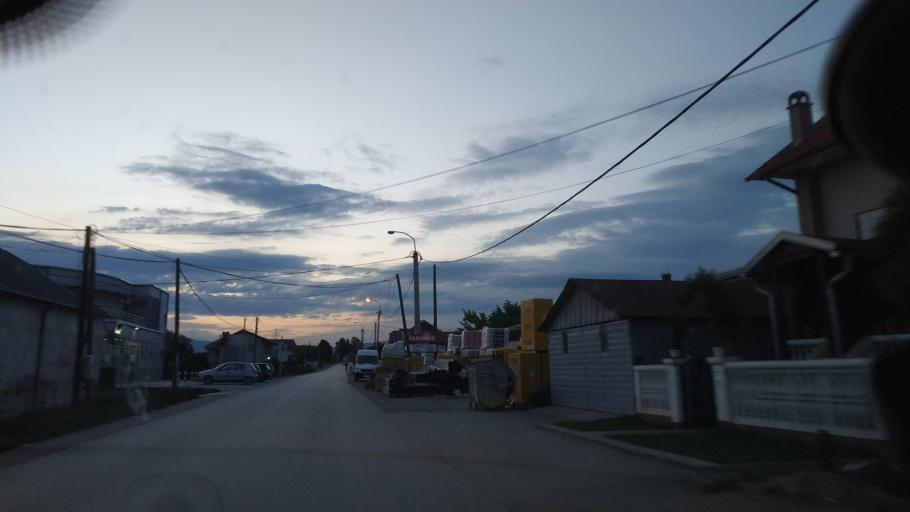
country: RS
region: Central Serbia
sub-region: Nisavski Okrug
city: Merosina
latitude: 43.2841
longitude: 21.7212
